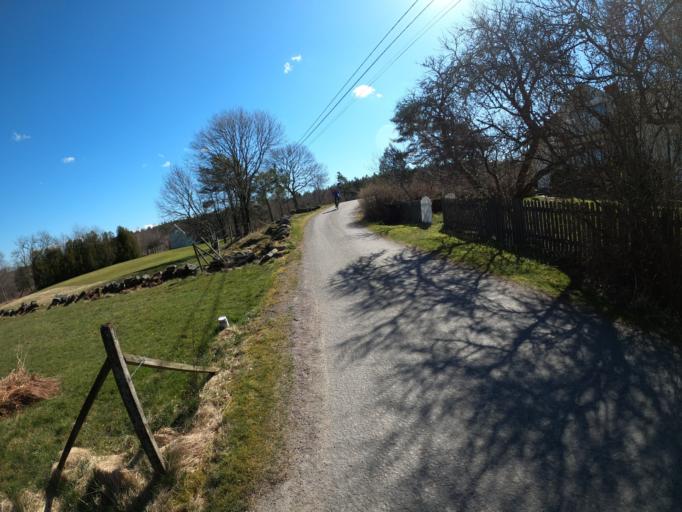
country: SE
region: Vaestra Goetaland
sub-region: Harryda Kommun
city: Molnlycke
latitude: 57.6308
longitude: 12.1208
